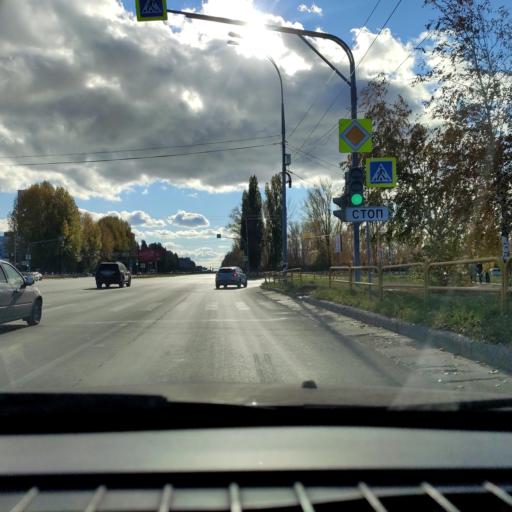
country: RU
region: Samara
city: Tol'yatti
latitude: 53.5156
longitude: 49.2781
